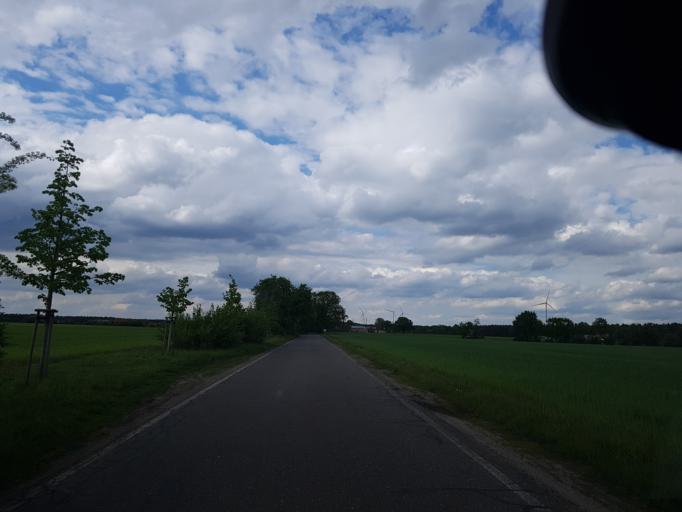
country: DE
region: Brandenburg
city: Grossraschen
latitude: 51.5798
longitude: 14.0623
